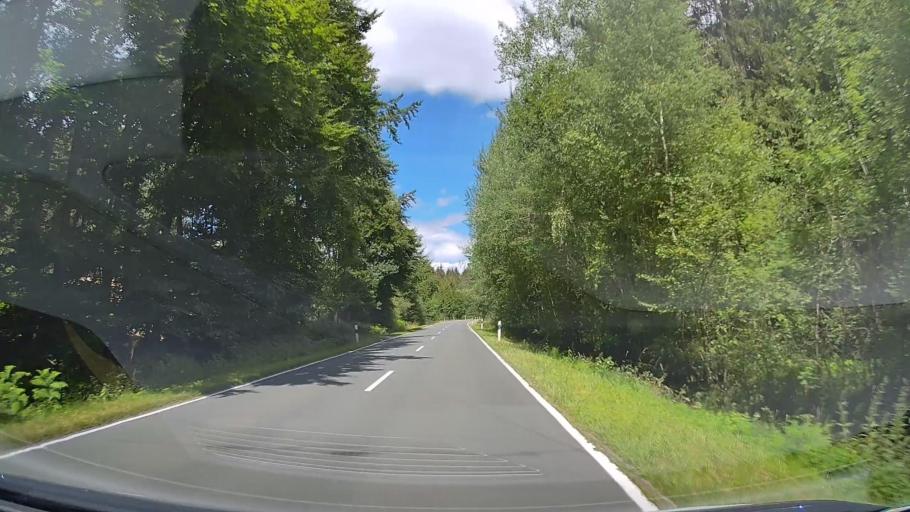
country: DE
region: Lower Saxony
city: Belm
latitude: 52.3493
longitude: 8.1390
